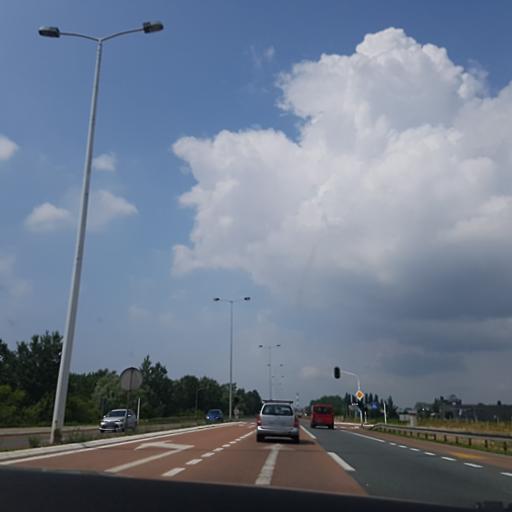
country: RS
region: Central Serbia
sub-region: Belgrade
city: Palilula
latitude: 44.8443
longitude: 20.5098
